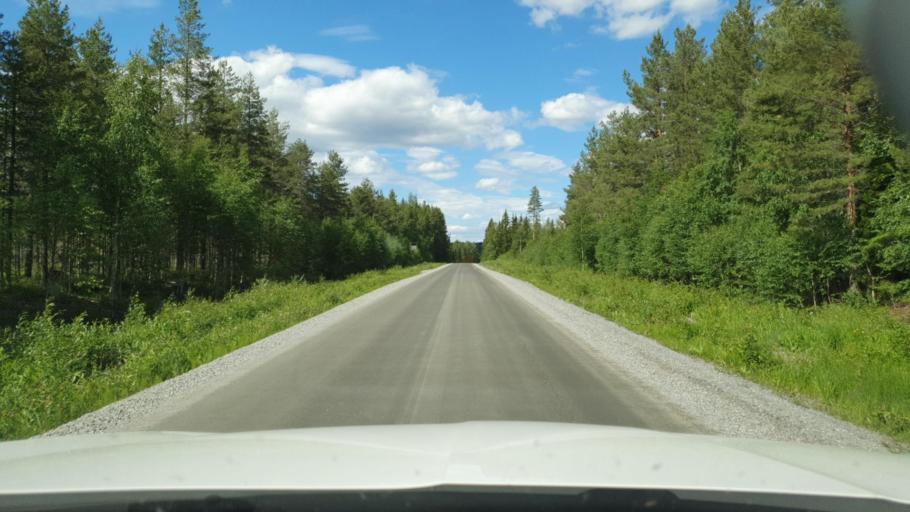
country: SE
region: Vaesterbotten
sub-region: Skelleftea Kommun
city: Forsbacka
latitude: 64.8069
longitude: 20.4994
